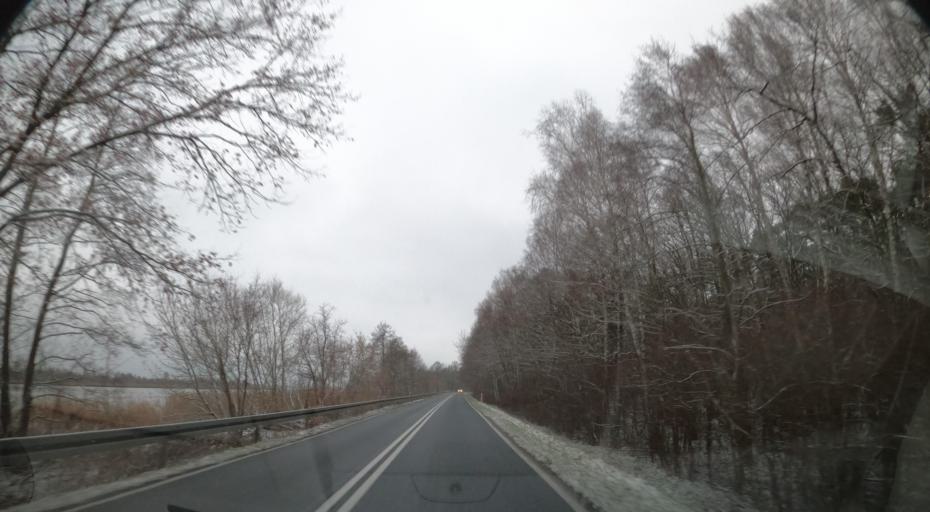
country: PL
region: Masovian Voivodeship
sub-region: Powiat plocki
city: Nowy Duninow
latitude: 52.5752
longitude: 19.5519
